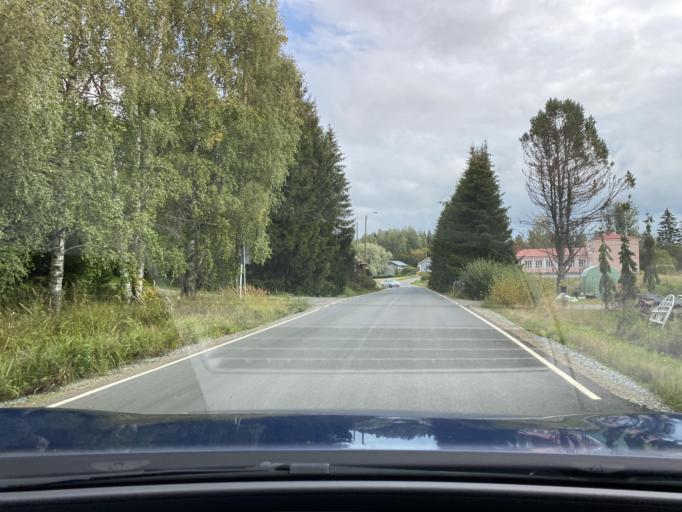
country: FI
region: Pirkanmaa
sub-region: Lounais-Pirkanmaa
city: Punkalaidun
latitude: 61.2334
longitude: 23.1228
